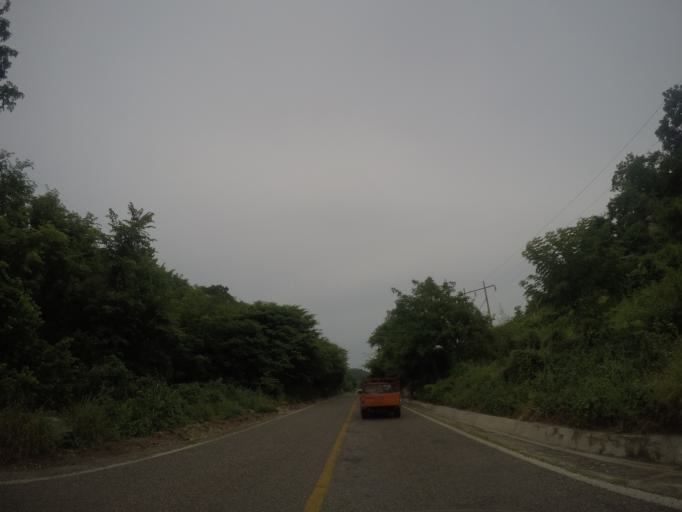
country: MX
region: Oaxaca
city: San Pedro Mixtepec
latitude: 15.9569
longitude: -97.2140
